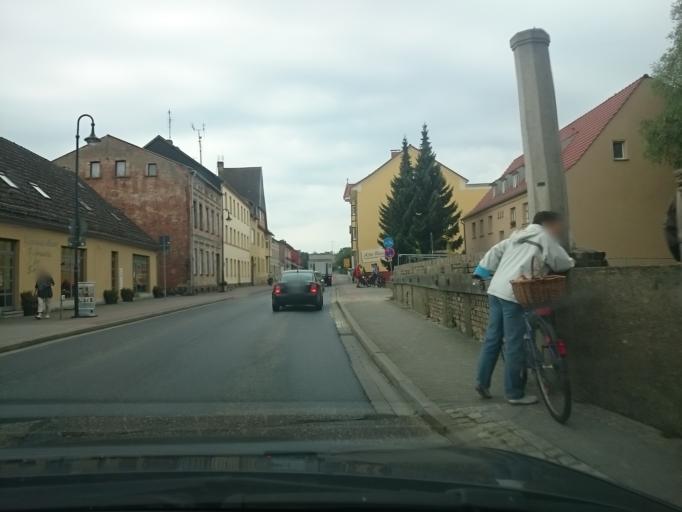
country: DE
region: Brandenburg
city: Furstenberg
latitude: 53.1833
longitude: 13.1452
